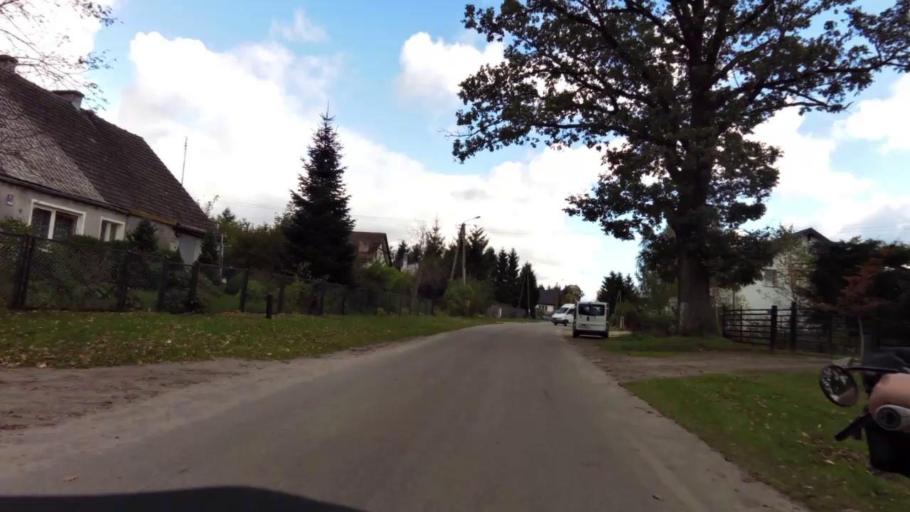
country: PL
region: West Pomeranian Voivodeship
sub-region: Powiat bialogardzki
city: Bialogard
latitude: 54.0377
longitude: 16.0553
